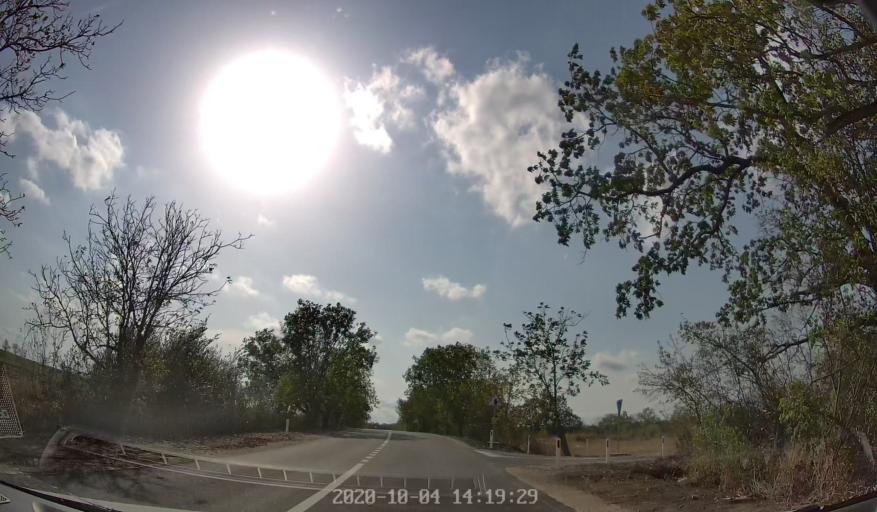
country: MD
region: Rezina
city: Saharna
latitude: 47.5907
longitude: 28.9729
